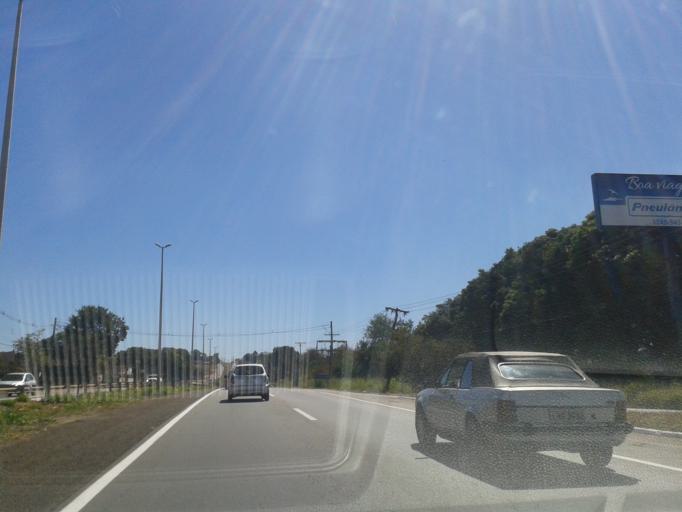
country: BR
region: Goias
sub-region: Goiania
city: Goiania
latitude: -16.6392
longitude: -49.3428
